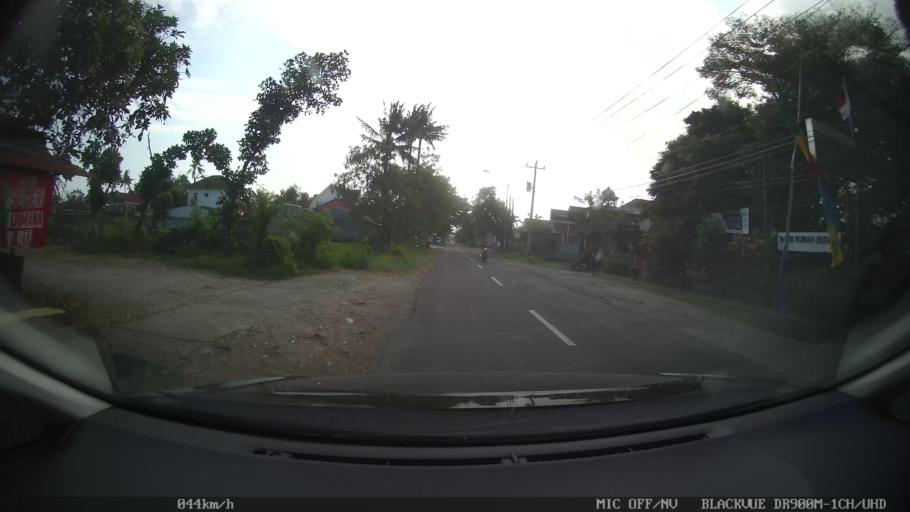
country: ID
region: Daerah Istimewa Yogyakarta
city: Sewon
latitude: -7.8705
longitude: 110.3567
